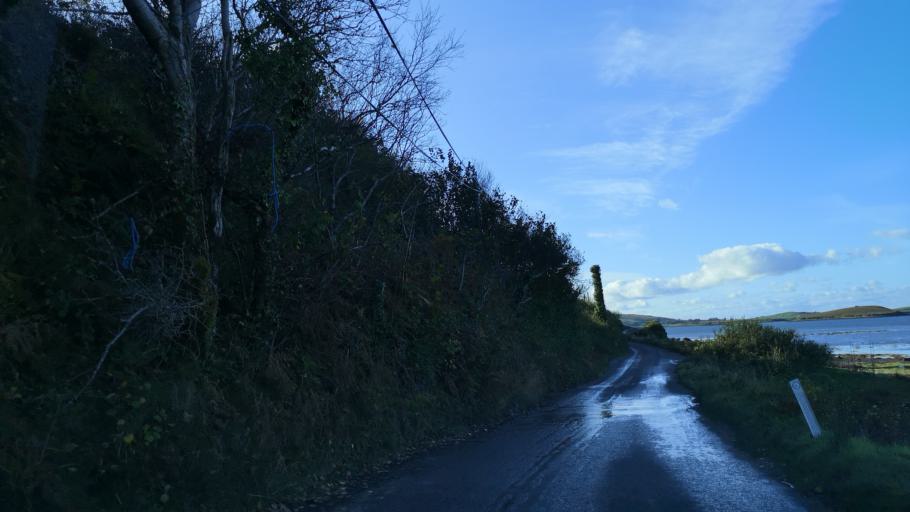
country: IE
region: Connaught
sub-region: County Galway
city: Clifden
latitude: 53.5053
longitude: -10.0463
